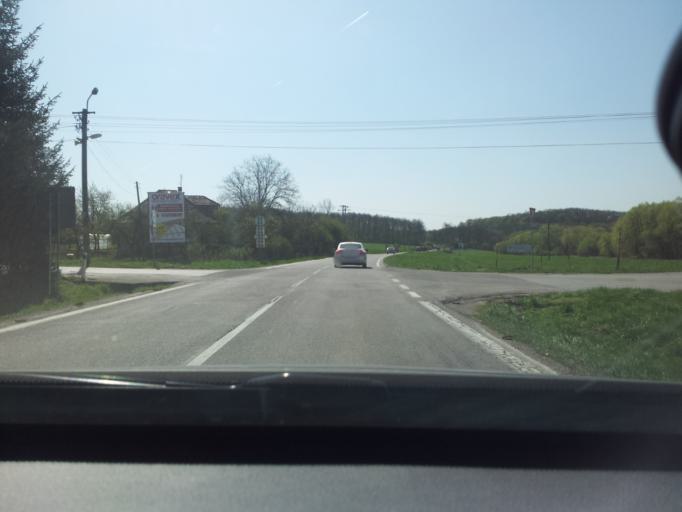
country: SK
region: Nitriansky
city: Banovce nad Bebravou
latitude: 48.7800
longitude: 18.1785
